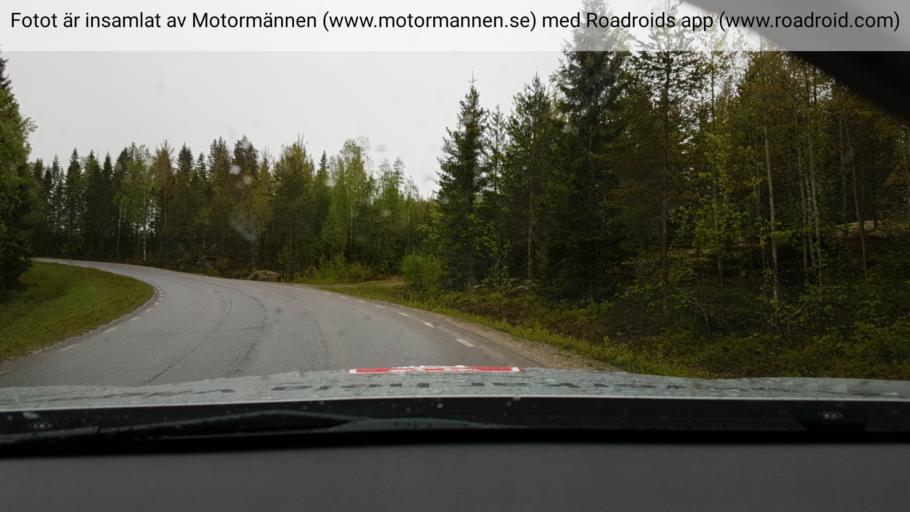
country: SE
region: Vaesterbotten
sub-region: Vannas Kommun
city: Vaennaes
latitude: 63.8885
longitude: 19.6871
